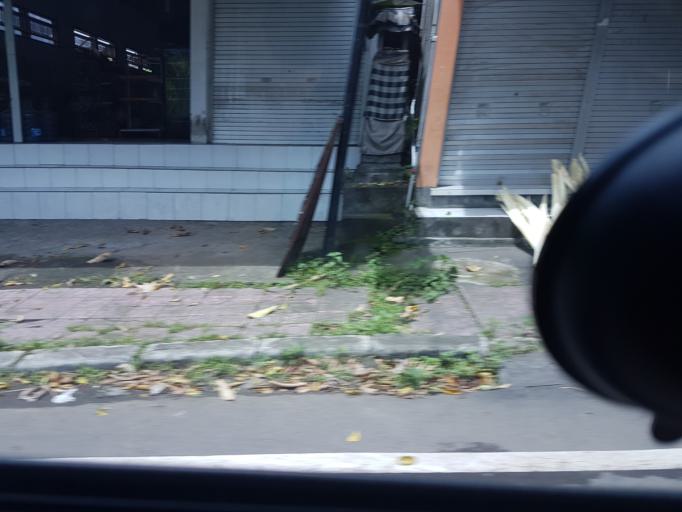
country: ID
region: Bali
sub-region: Kabupaten Gianyar
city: Ubud
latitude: -8.5101
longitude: 115.2934
